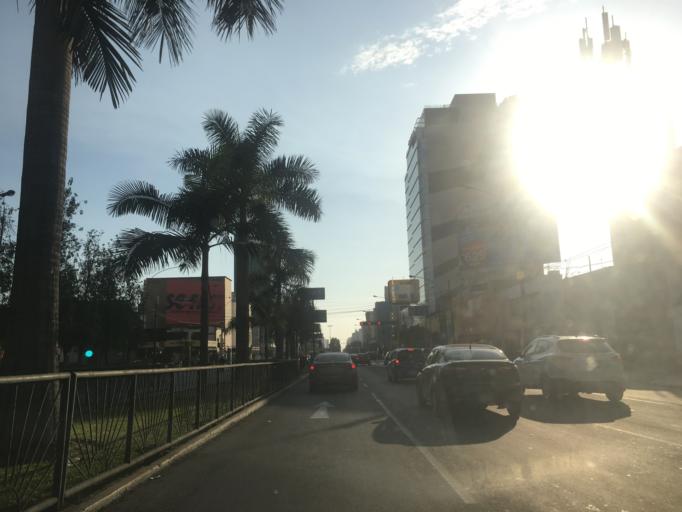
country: PE
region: Lima
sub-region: Lima
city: San Isidro
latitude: -12.0919
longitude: -77.0315
